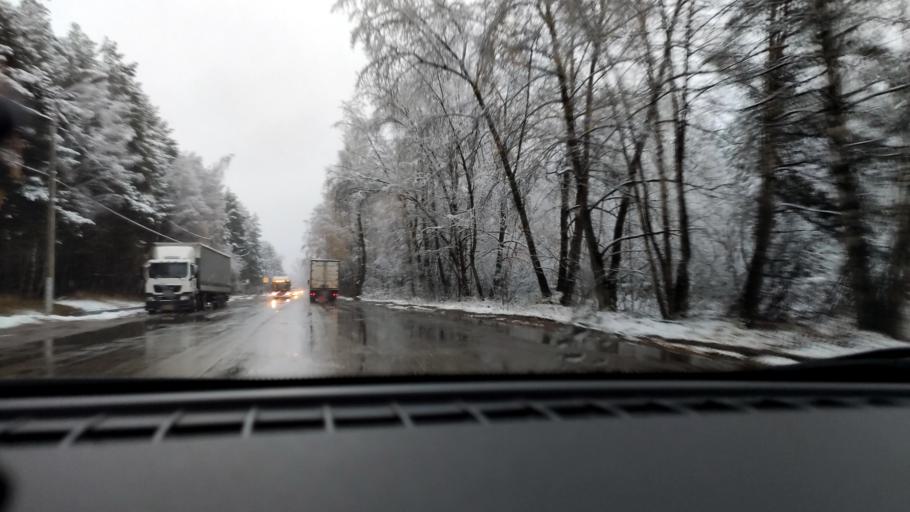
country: RU
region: Perm
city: Overyata
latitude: 58.0136
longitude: 55.9147
